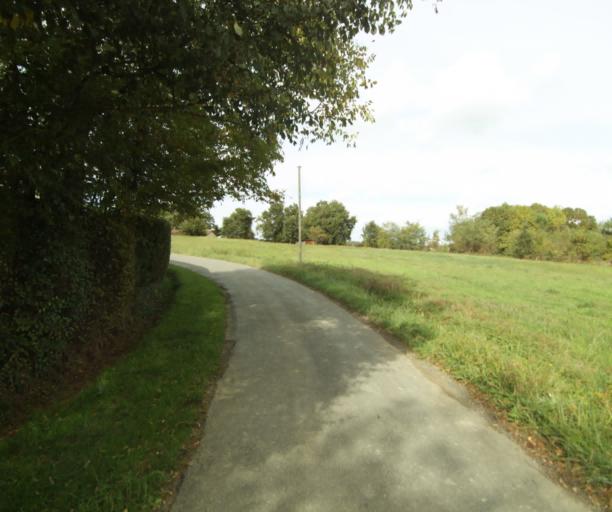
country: FR
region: Midi-Pyrenees
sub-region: Departement du Gers
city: Eauze
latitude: 43.8553
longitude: 0.0739
